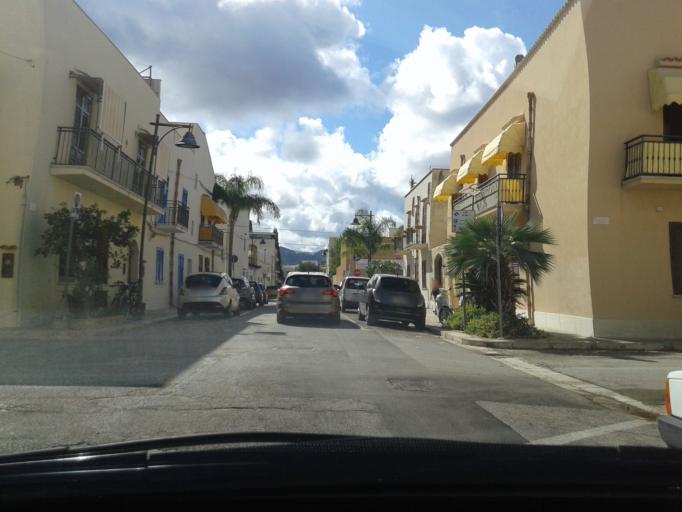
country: IT
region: Sicily
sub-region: Trapani
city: San Vito Lo Capo
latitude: 38.1729
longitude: 12.7345
